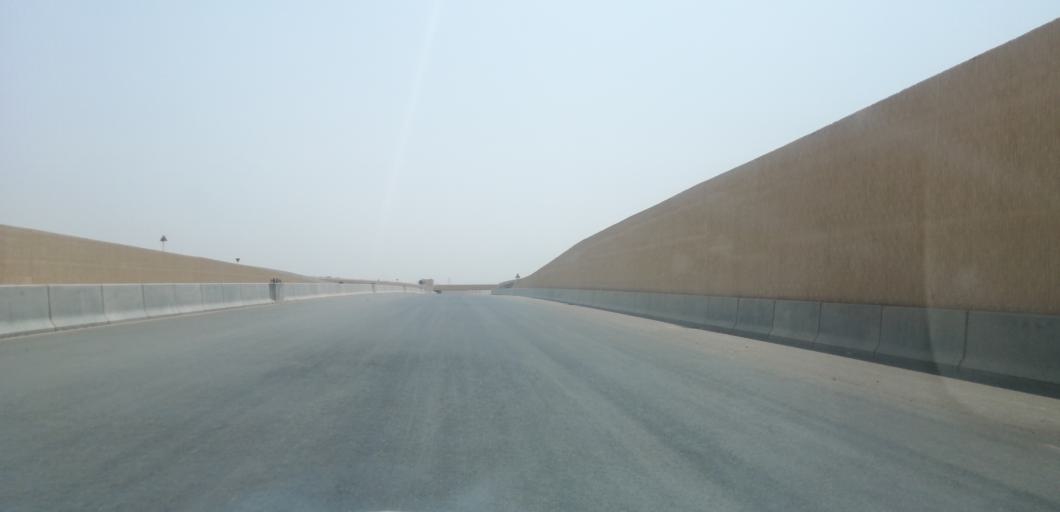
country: KW
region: Muhafazat al Jahra'
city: Al Jahra'
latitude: 29.4528
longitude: 47.5911
